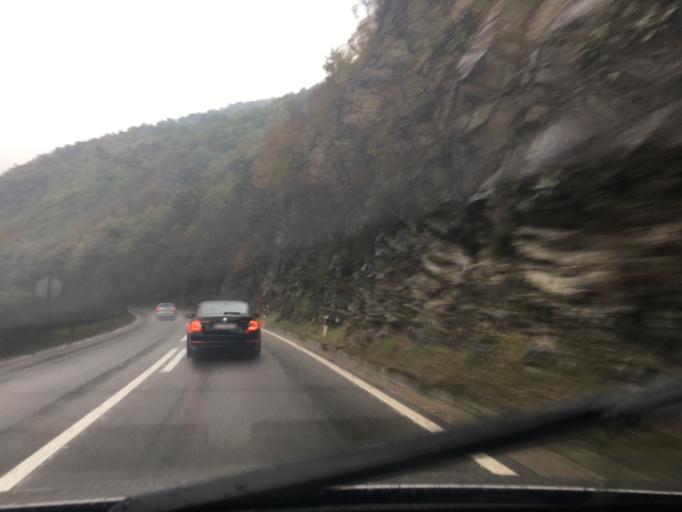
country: RS
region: Central Serbia
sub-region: Pcinjski Okrug
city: Vladicin Han
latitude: 42.7309
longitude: 22.0664
